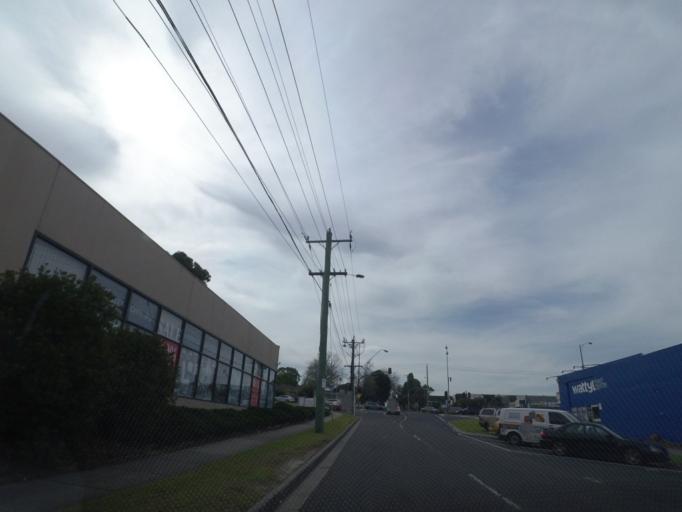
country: AU
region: Victoria
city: Mitcham
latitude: -37.8168
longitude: 145.2020
